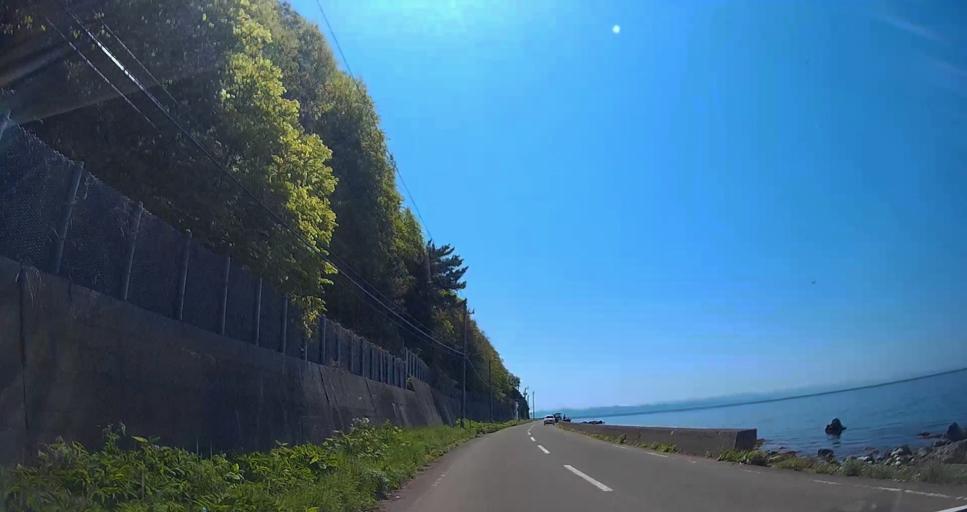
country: JP
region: Aomori
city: Aomori Shi
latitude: 41.1319
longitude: 140.7951
